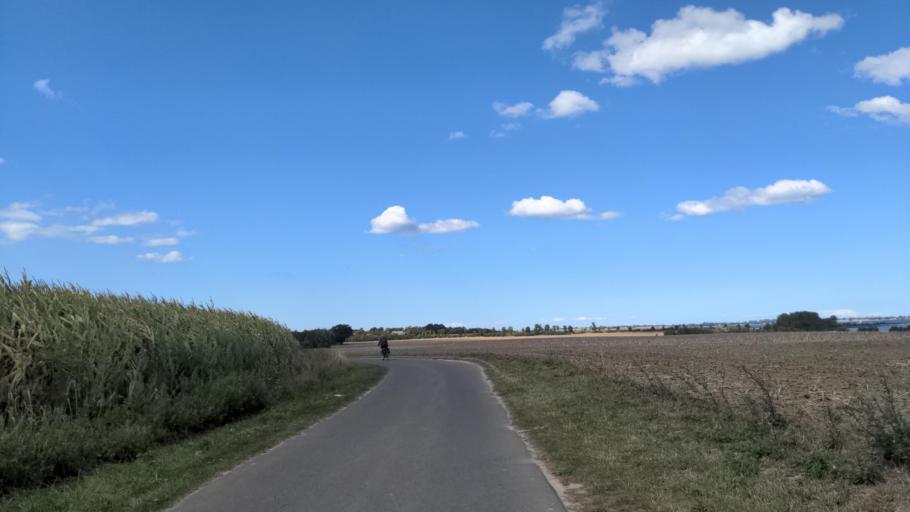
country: DE
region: Mecklenburg-Vorpommern
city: Wismar
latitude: 53.9198
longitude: 11.3982
